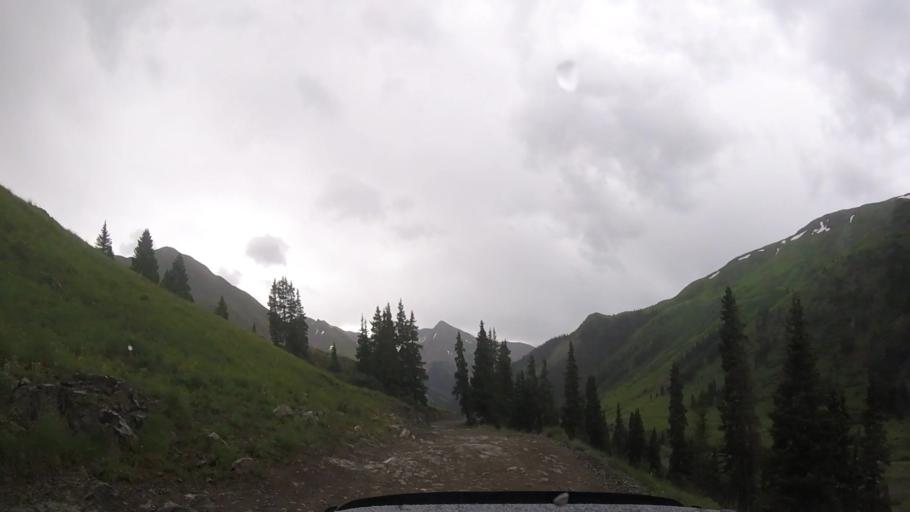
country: US
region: Colorado
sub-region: Ouray County
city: Ouray
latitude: 37.9323
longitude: -107.5677
